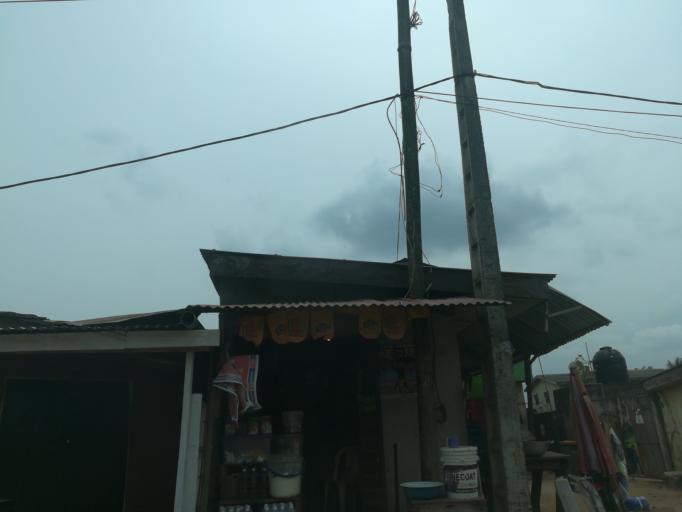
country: NG
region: Lagos
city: Ojota
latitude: 6.6090
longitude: 3.4145
